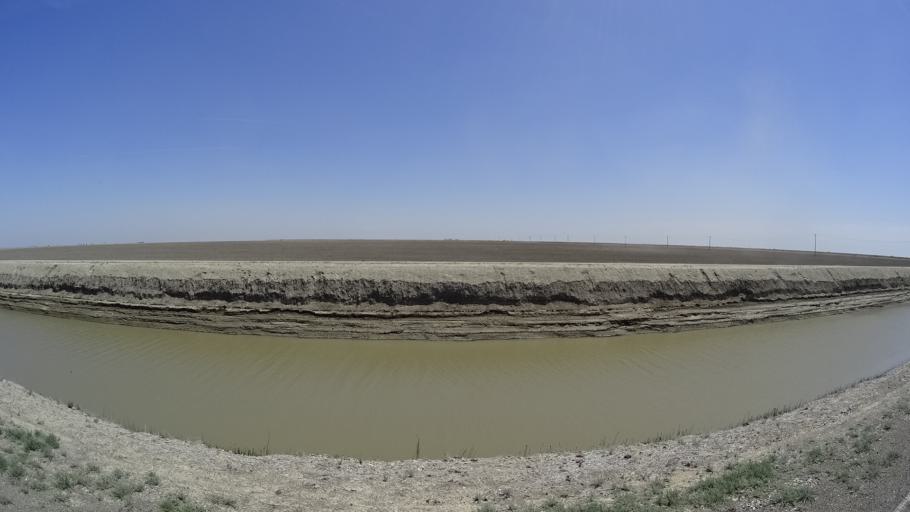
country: US
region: California
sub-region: Kings County
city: Corcoran
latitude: 35.9510
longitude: -119.6458
